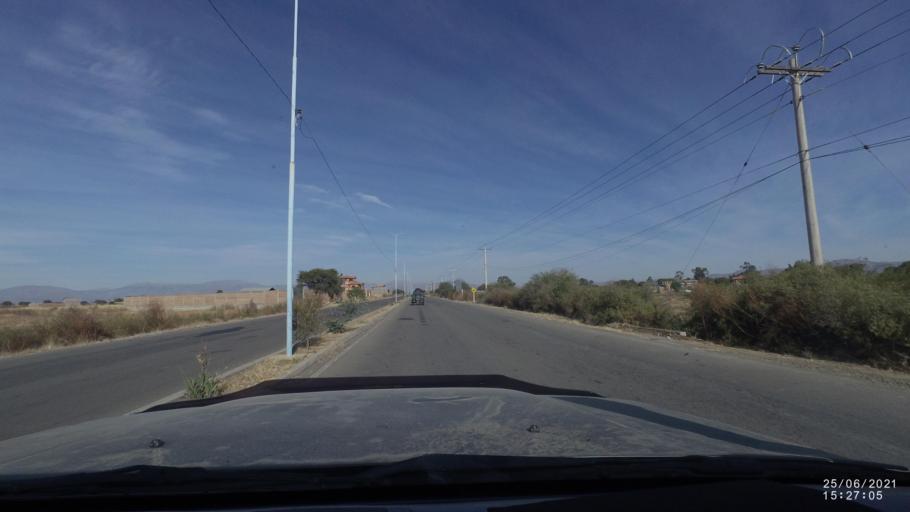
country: BO
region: Cochabamba
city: Cliza
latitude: -17.5458
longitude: -65.9530
